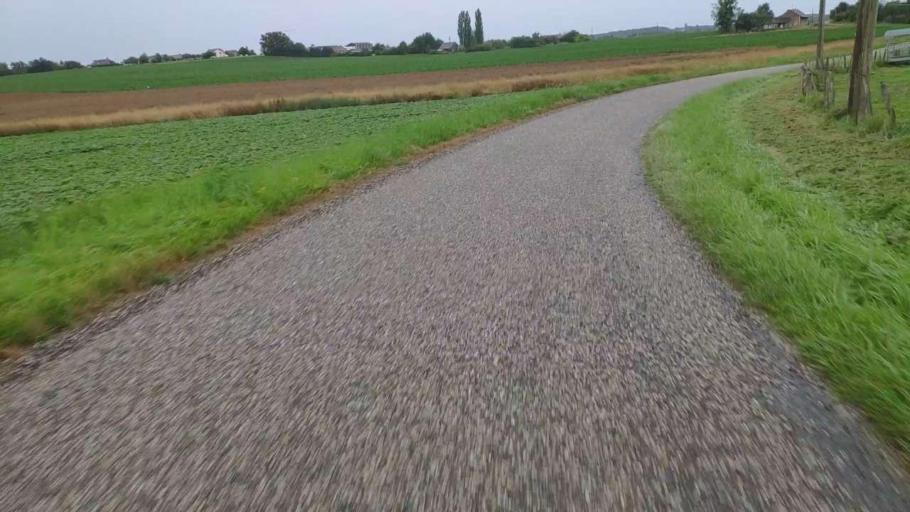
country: FR
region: Franche-Comte
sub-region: Departement du Jura
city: Chaussin
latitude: 46.8744
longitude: 5.4163
